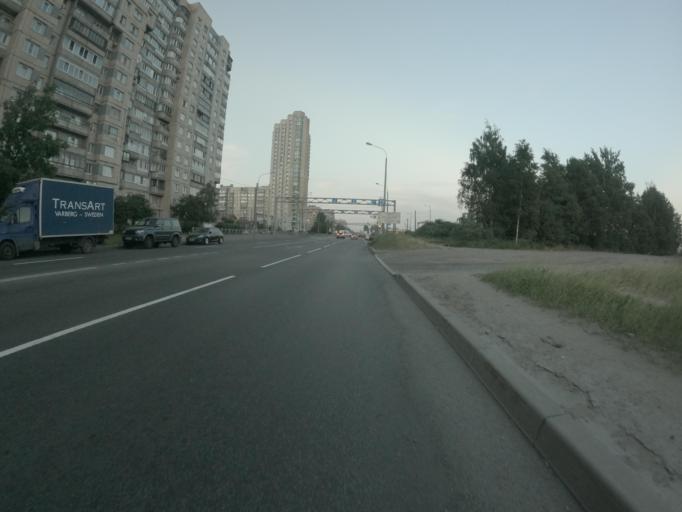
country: RU
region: St.-Petersburg
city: Krasnogvargeisky
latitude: 59.9372
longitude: 30.4736
